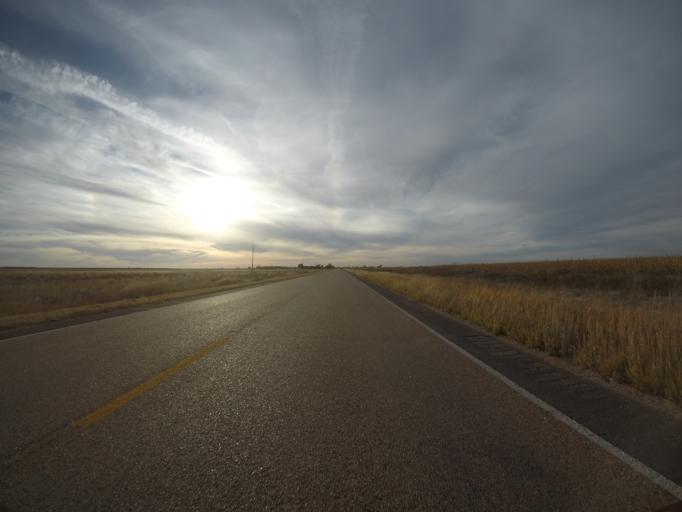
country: US
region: Colorado
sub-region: Yuma County
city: Yuma
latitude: 39.6562
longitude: -102.6125
